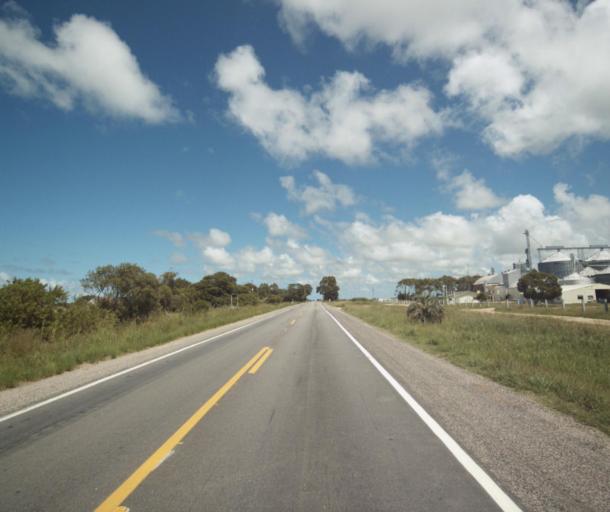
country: UY
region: Cerro Largo
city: Rio Branco
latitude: -32.8863
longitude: -52.7218
